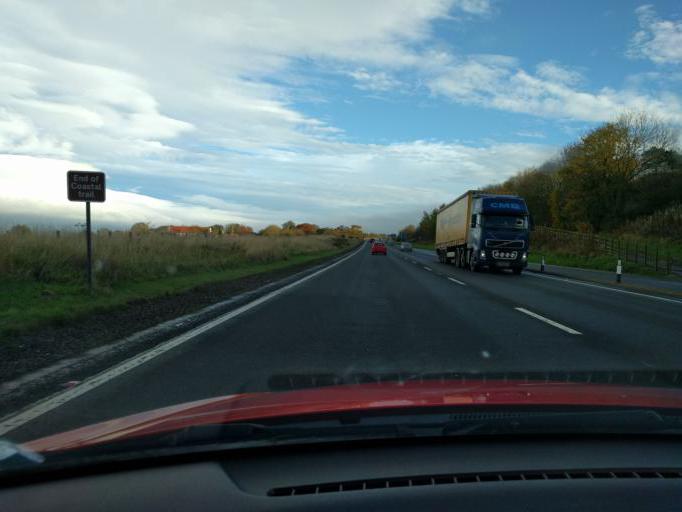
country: GB
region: Scotland
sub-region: East Lothian
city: Dunbar
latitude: 55.9437
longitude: -2.3727
